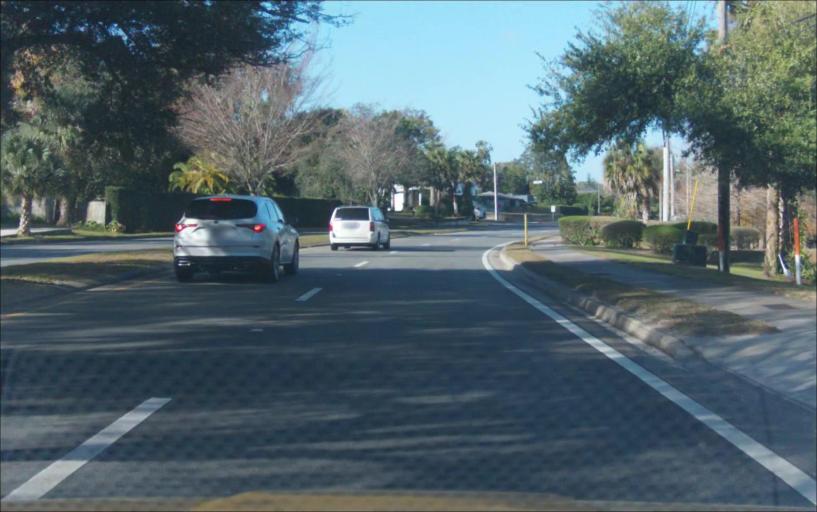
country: US
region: Florida
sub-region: Orange County
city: Maitland
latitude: 28.6264
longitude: -81.3493
